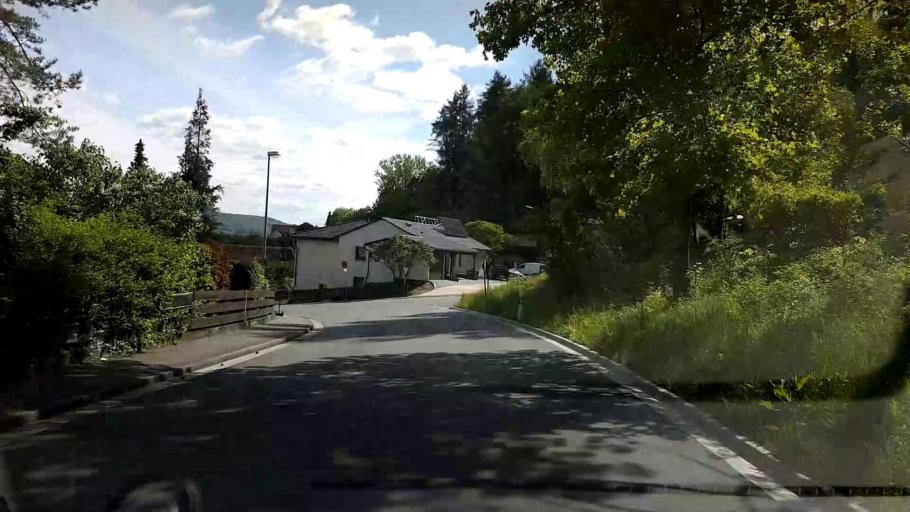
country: DE
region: Bavaria
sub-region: Upper Franconia
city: Ebermannstadt
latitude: 49.7827
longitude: 11.1744
